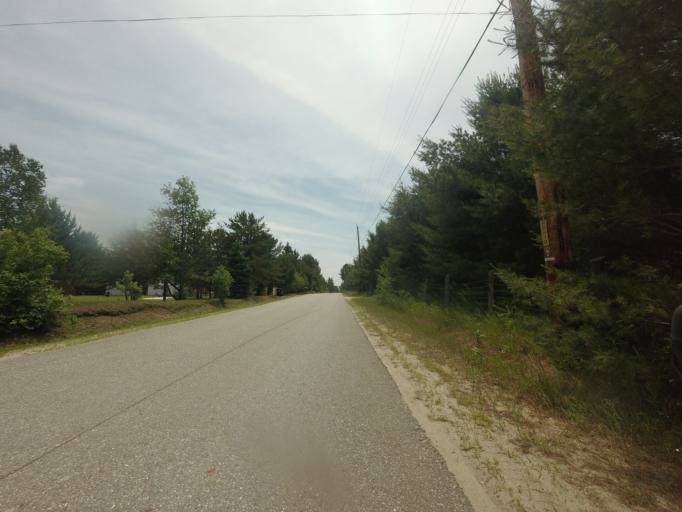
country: CA
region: Quebec
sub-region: Outaouais
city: Wakefield
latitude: 45.9551
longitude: -76.0604
